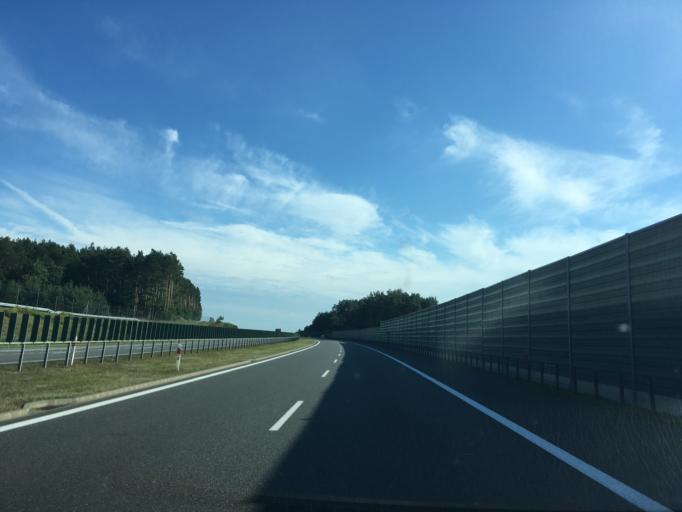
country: PL
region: Kujawsko-Pomorskie
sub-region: Powiat swiecki
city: Warlubie
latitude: 53.4628
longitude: 18.6220
